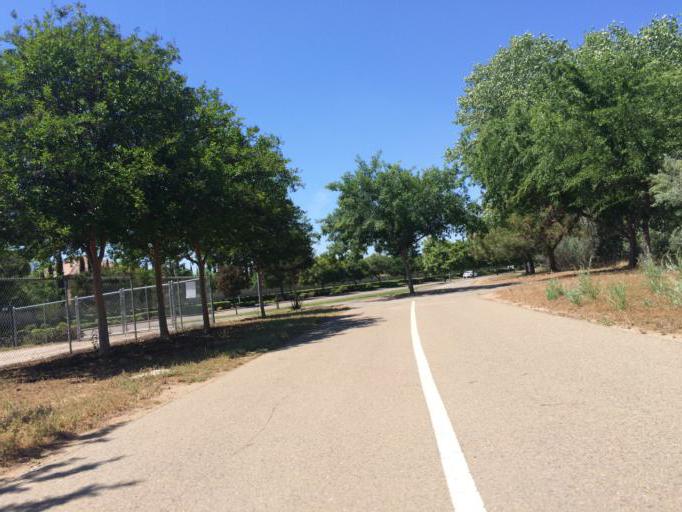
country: US
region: California
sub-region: Fresno County
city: Clovis
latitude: 36.8492
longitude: -119.7019
